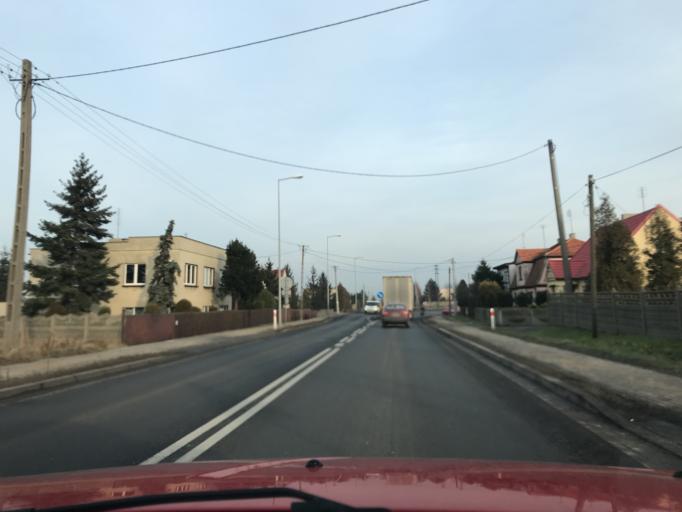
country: PL
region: Greater Poland Voivodeship
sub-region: Powiat pleszewski
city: Pleszew
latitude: 51.8997
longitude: 17.7973
